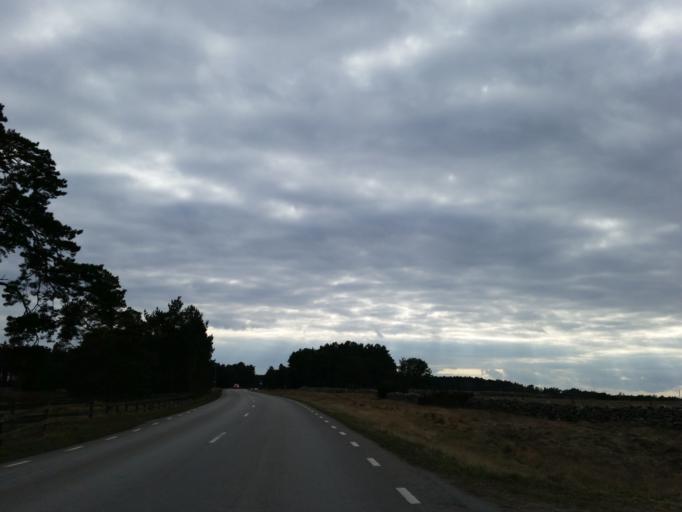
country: SE
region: Kalmar
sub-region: Morbylanga Kommun
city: Sodra Sandby
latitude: 56.5904
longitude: 16.6314
